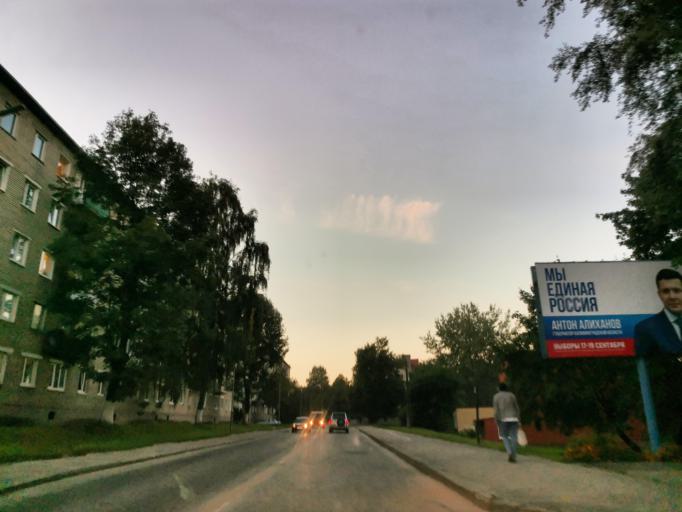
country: RU
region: Kaliningrad
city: Chernyakhovsk
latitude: 54.6365
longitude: 21.8032
